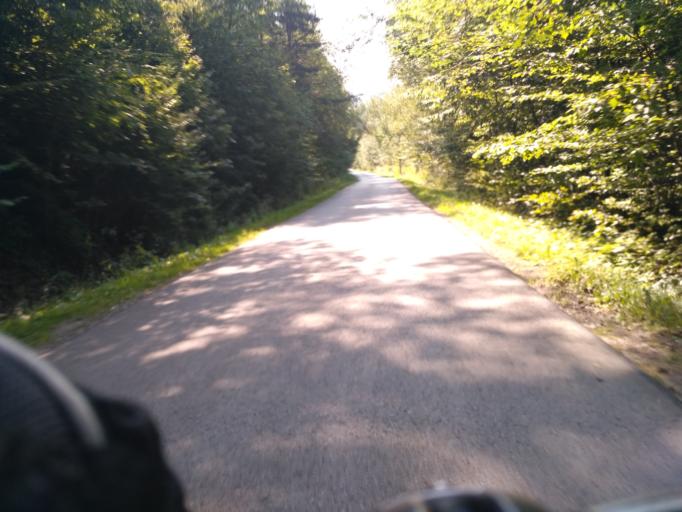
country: PL
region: Subcarpathian Voivodeship
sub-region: Powiat brzozowski
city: Golcowa
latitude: 49.7934
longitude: 22.0191
